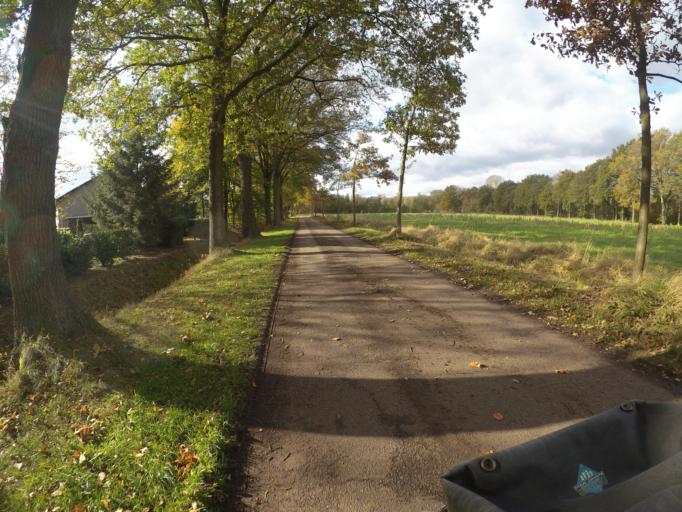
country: NL
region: North Brabant
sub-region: Gemeente Boxtel
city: Boxtel
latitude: 51.5602
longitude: 5.2958
